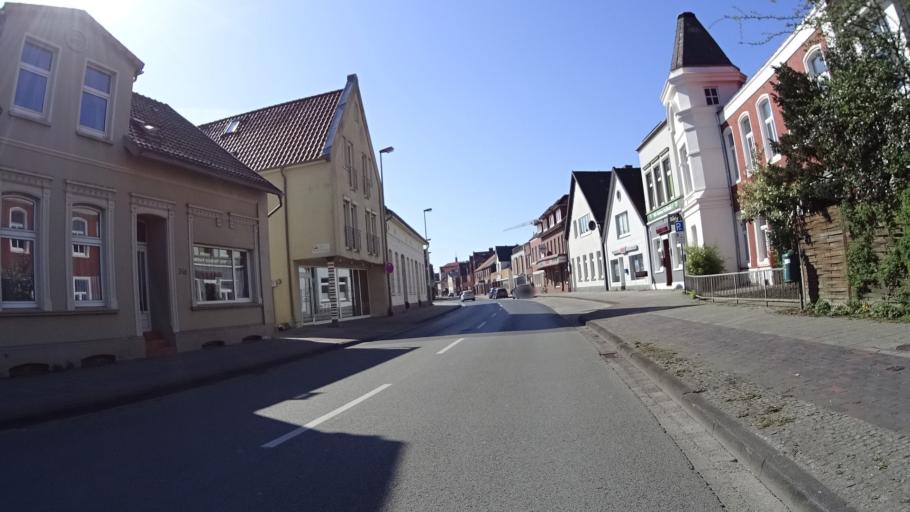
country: DE
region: Lower Saxony
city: Leer
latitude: 53.2321
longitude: 7.4517
